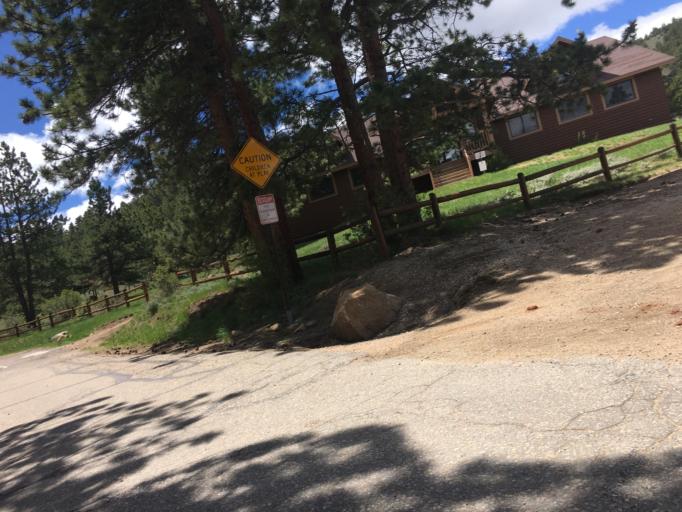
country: US
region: Colorado
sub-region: Larimer County
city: Estes Park
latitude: 40.3417
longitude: -105.5794
